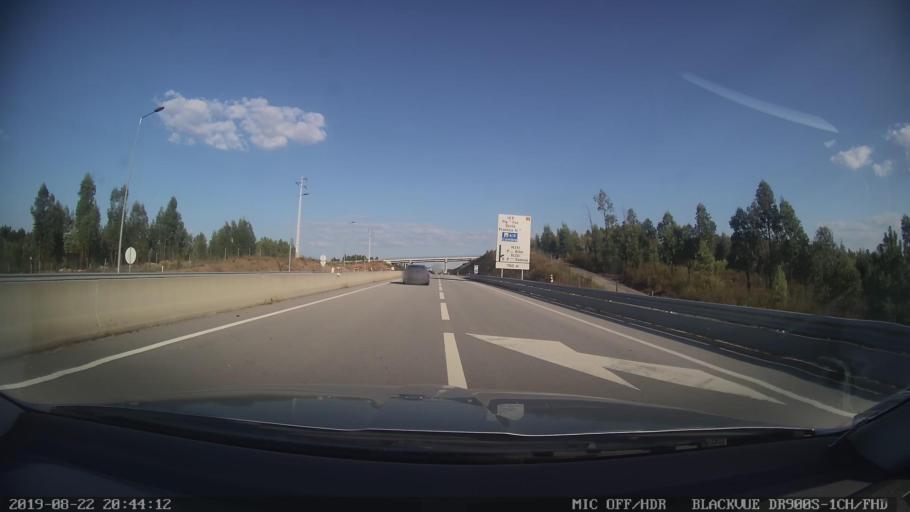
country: PT
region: Castelo Branco
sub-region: Proenca-A-Nova
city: Proenca-a-Nova
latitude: 39.7053
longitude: -7.8471
